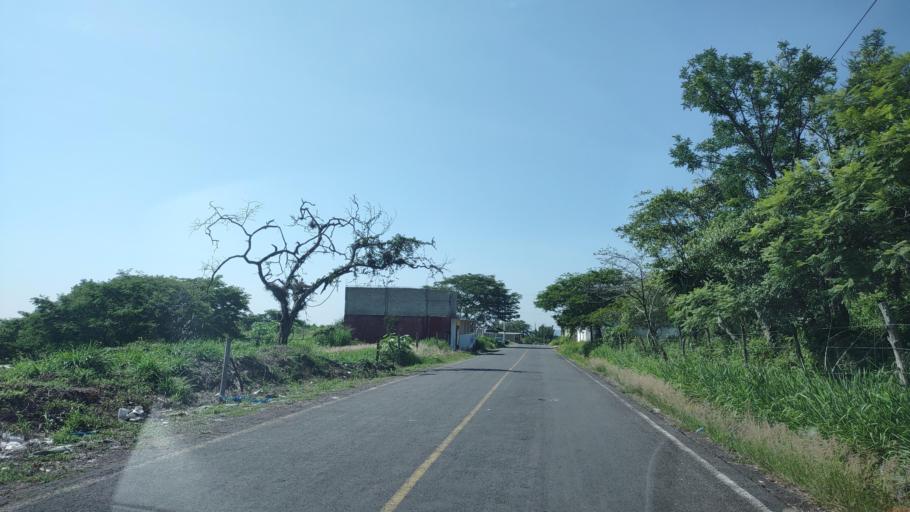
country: MX
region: Veracruz
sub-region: Emiliano Zapata
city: Dos Rios
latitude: 19.4921
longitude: -96.8224
